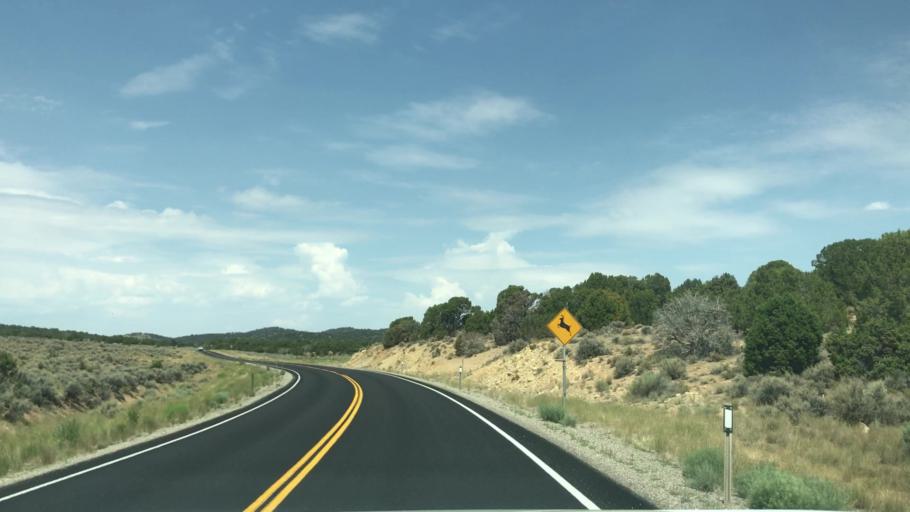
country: US
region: Nevada
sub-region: Eureka County
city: Eureka
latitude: 39.3886
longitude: -115.4487
